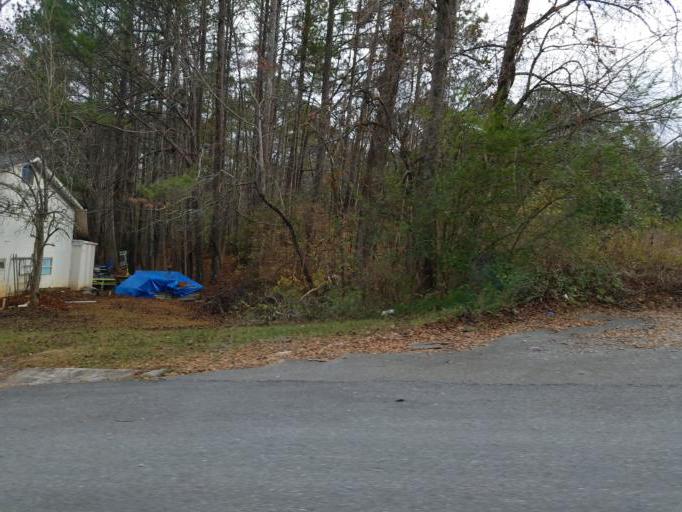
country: US
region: Georgia
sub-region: Cherokee County
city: Canton
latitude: 34.2151
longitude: -84.5179
